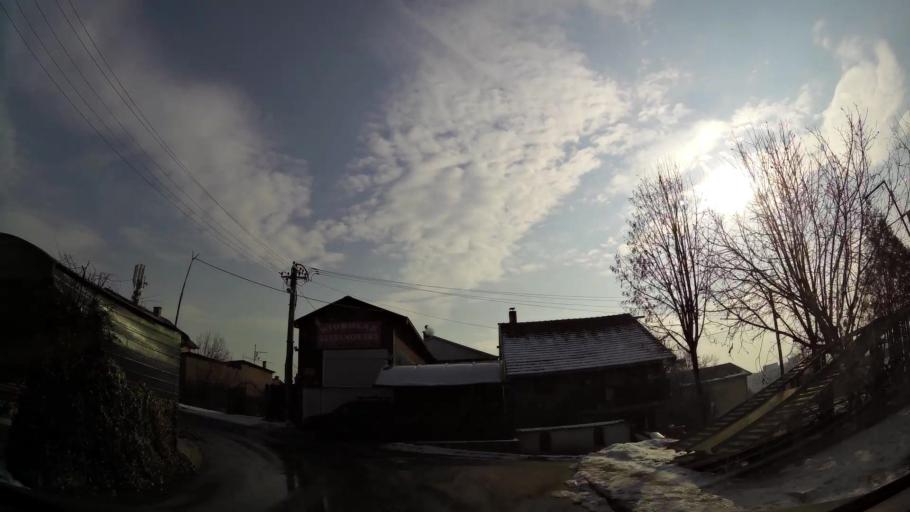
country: MK
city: Creshevo
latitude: 42.0048
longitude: 21.4957
